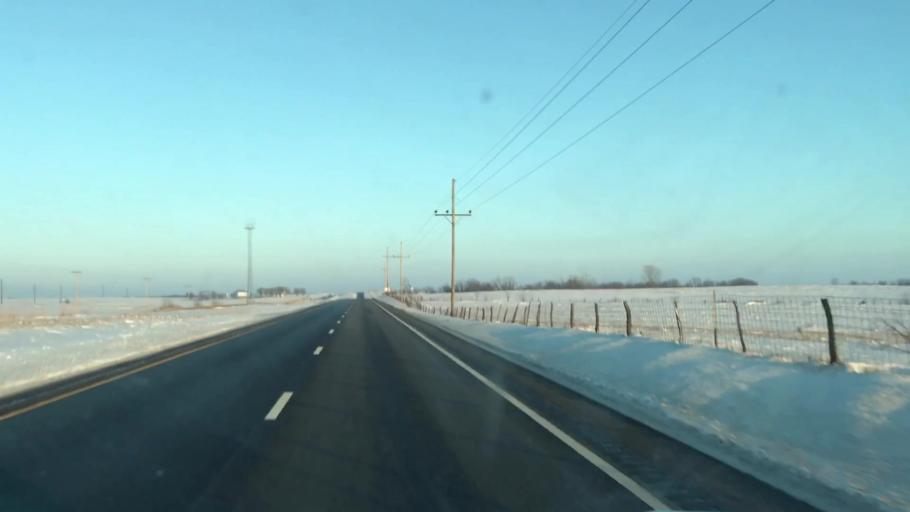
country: US
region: Missouri
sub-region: Clinton County
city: Cameron
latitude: 39.7542
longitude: -94.2908
